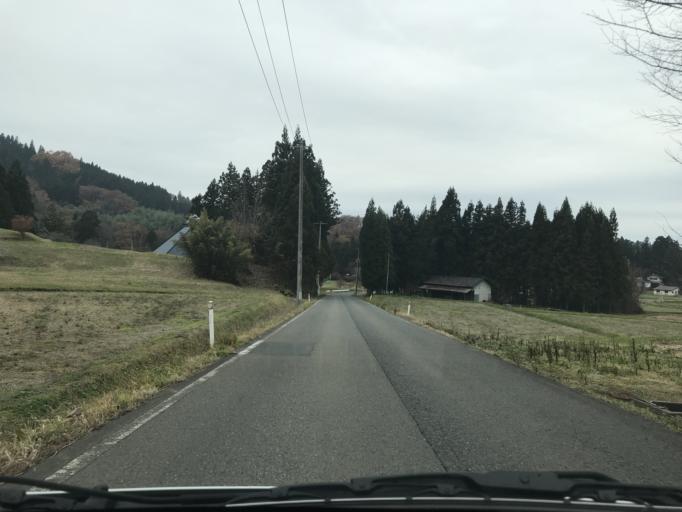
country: JP
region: Iwate
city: Kitakami
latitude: 39.2869
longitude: 141.1759
